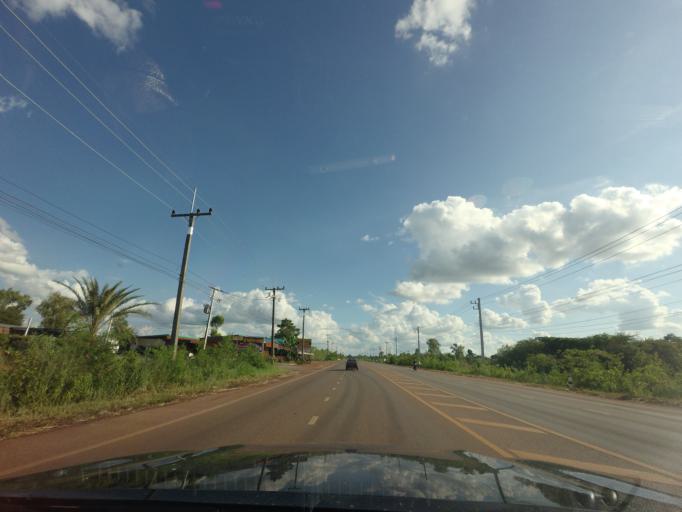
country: TH
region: Changwat Udon Thani
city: Ban Dung
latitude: 17.7214
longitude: 103.2502
